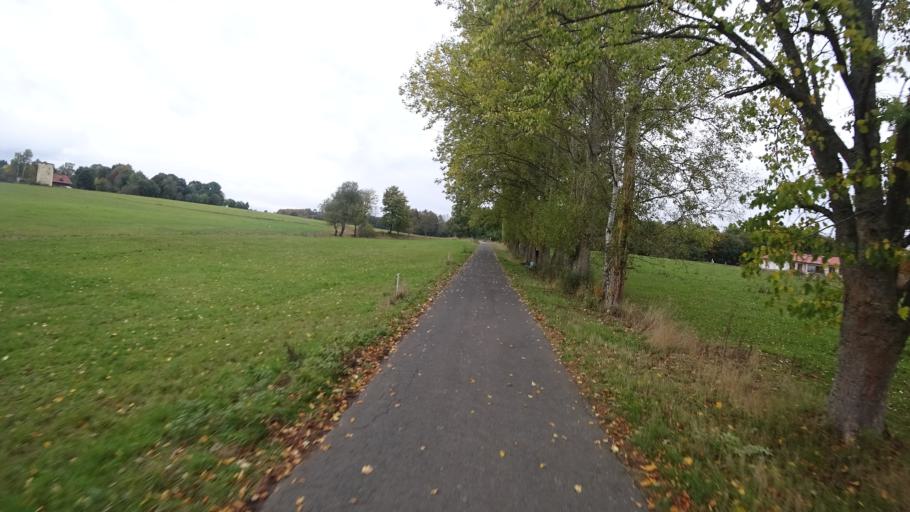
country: DE
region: Rheinland-Pfalz
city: Marienrachdorf
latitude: 50.5538
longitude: 7.7205
